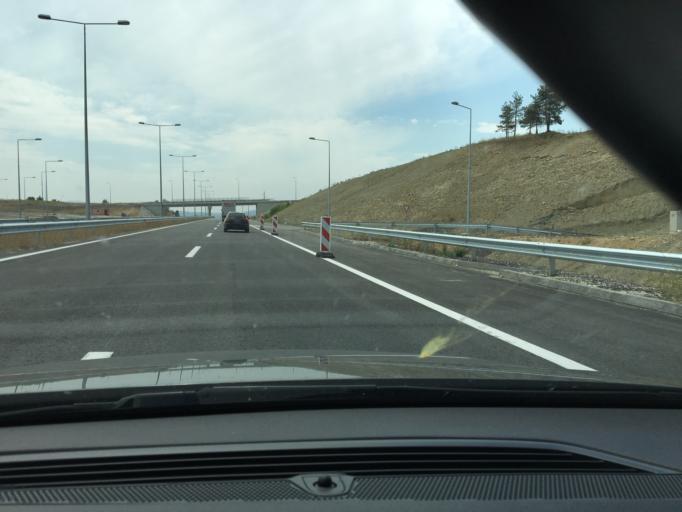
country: MK
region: Stip
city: Shtip
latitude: 41.7824
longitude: 22.1240
